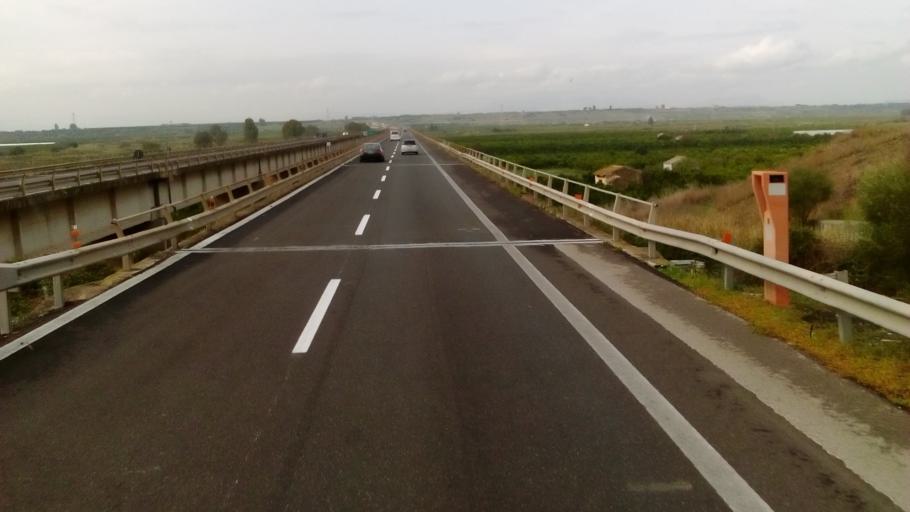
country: IT
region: Sicily
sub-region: Catania
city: Motta Sant'Anastasia
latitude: 37.4685
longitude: 14.9003
